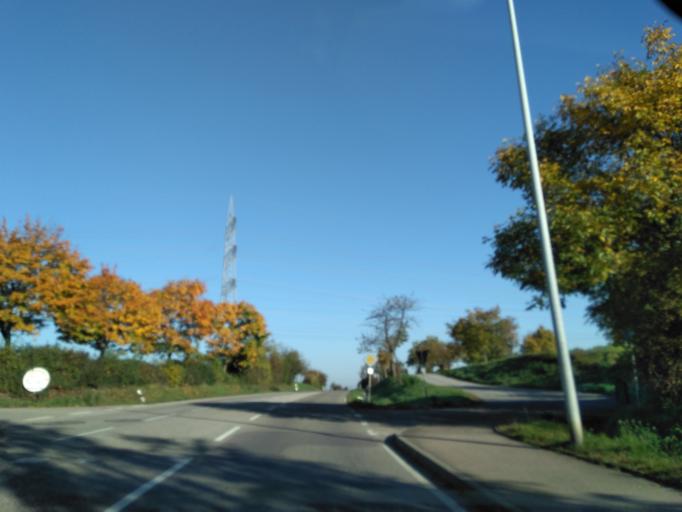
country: DE
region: Baden-Wuerttemberg
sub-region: Regierungsbezirk Stuttgart
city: Markgroningen
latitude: 48.9122
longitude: 9.0767
